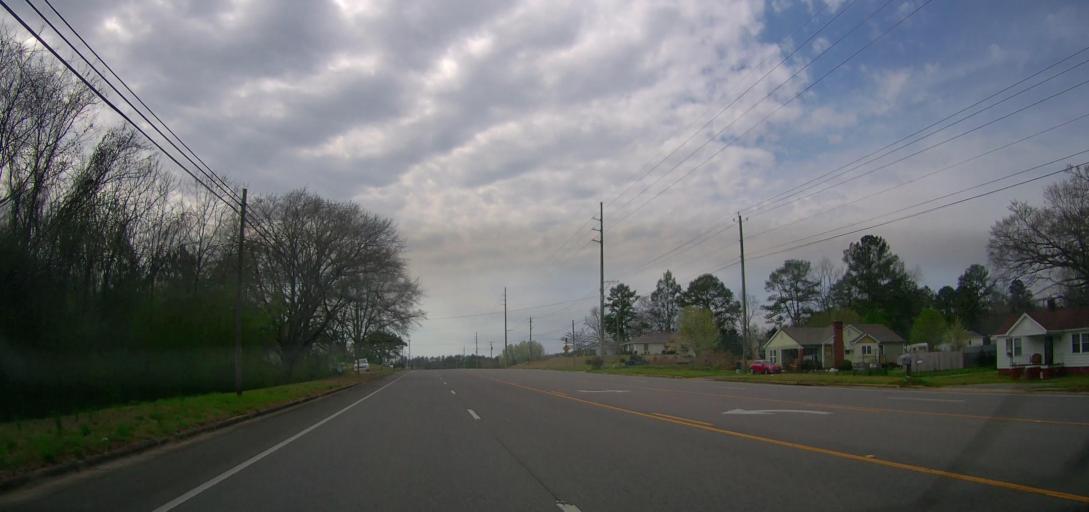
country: US
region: Alabama
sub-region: Marion County
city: Winfield
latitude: 33.9308
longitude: -87.7789
